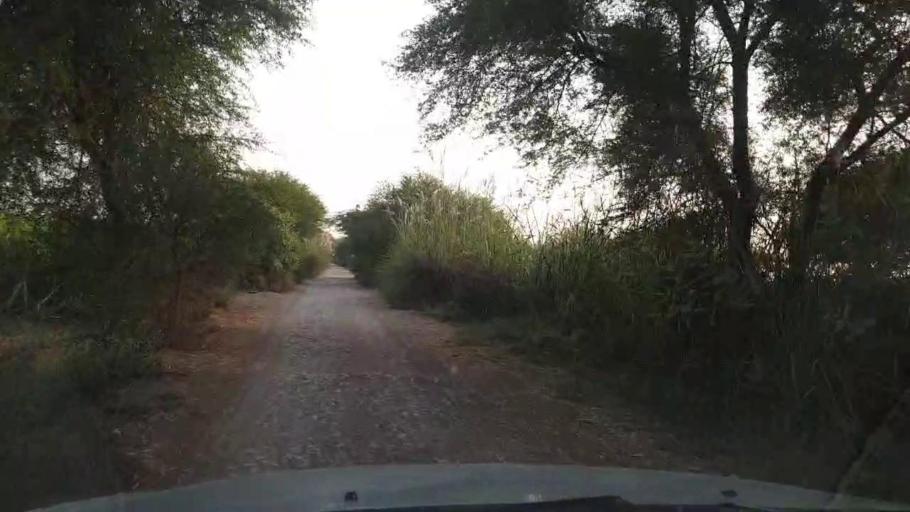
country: PK
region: Sindh
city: Tando Muhammad Khan
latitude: 25.0066
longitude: 68.4356
